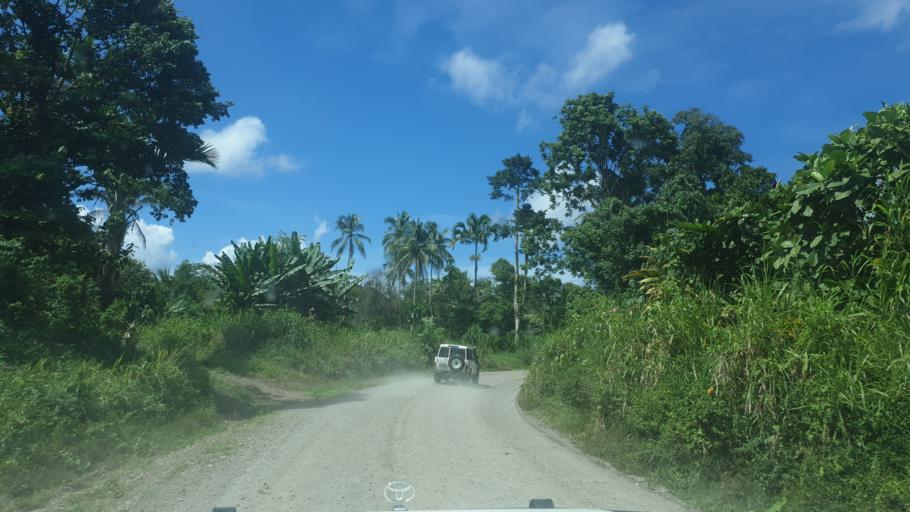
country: PG
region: Bougainville
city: Panguna
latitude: -6.7375
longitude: 155.6681
